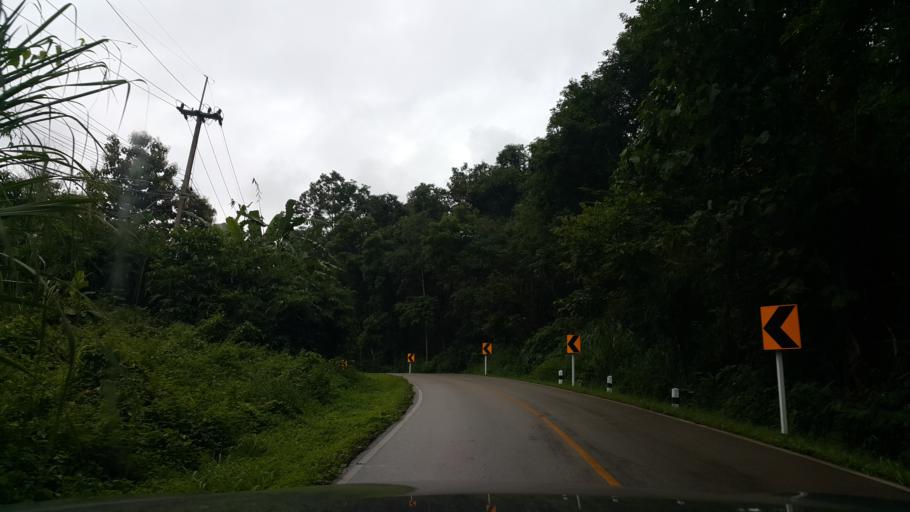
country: TH
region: Chiang Mai
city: Samoeng
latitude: 18.8640
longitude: 98.7140
